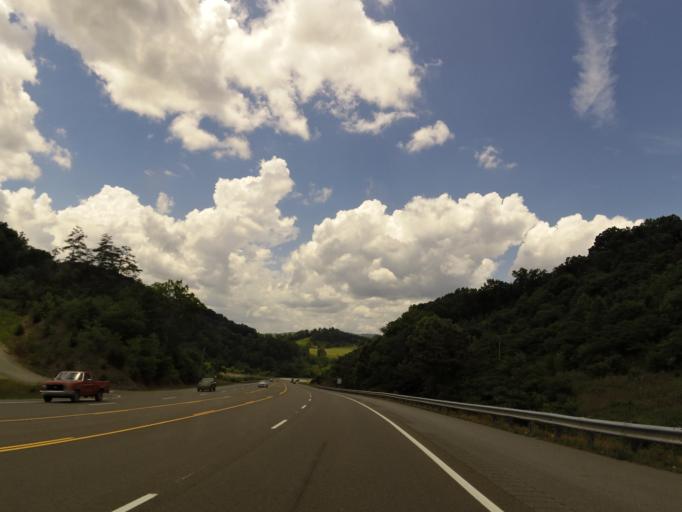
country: US
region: Tennessee
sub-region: Claiborne County
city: Harrogate
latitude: 36.5328
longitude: -83.6203
